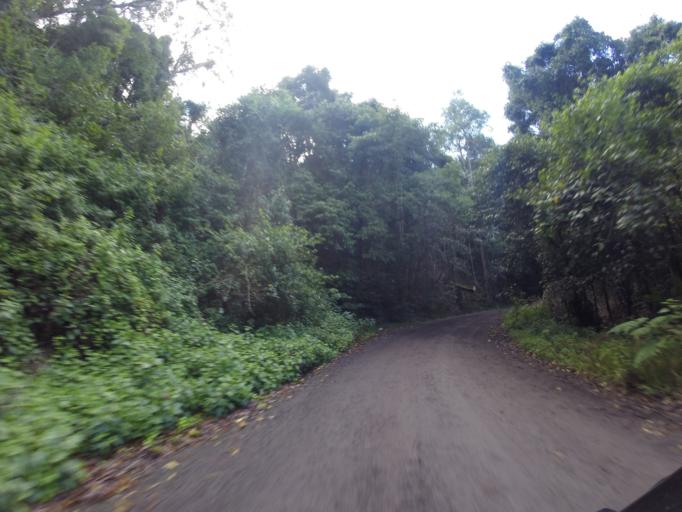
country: AU
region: New South Wales
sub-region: Wollongong
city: Cordeaux Heights
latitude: -34.4388
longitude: 150.7904
